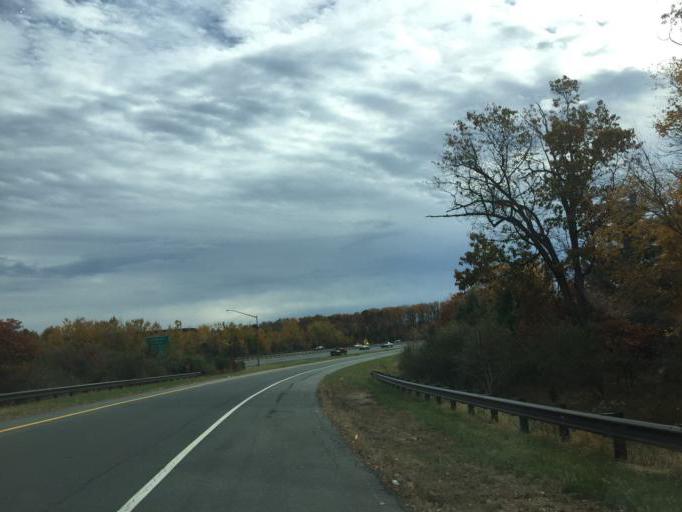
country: US
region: Maryland
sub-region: Montgomery County
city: Germantown
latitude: 39.1961
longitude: -77.2635
